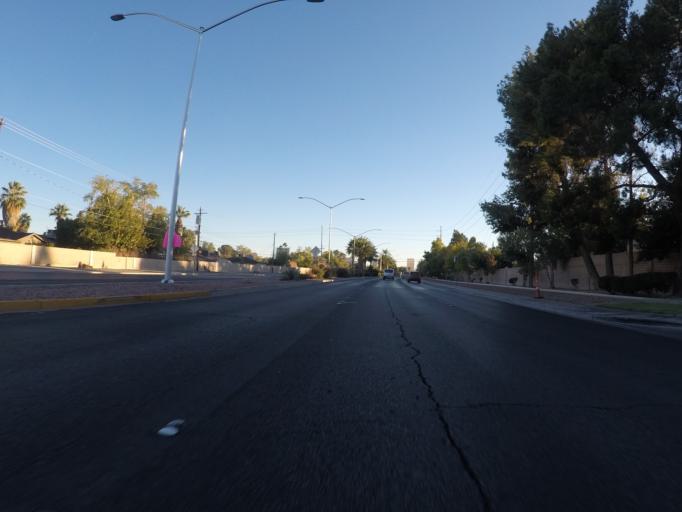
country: US
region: Nevada
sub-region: Clark County
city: Las Vegas
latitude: 36.1711
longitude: -115.1727
